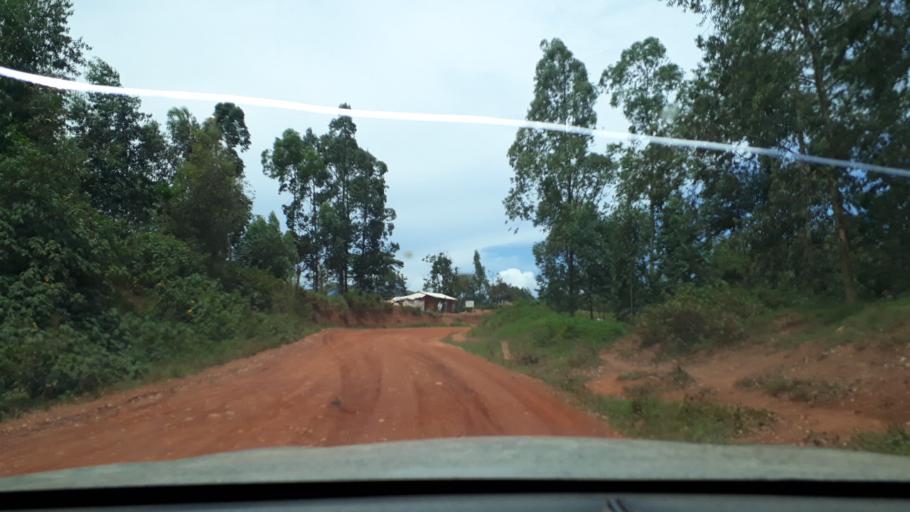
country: CD
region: Eastern Province
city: Bunia
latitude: 1.7269
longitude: 30.3172
